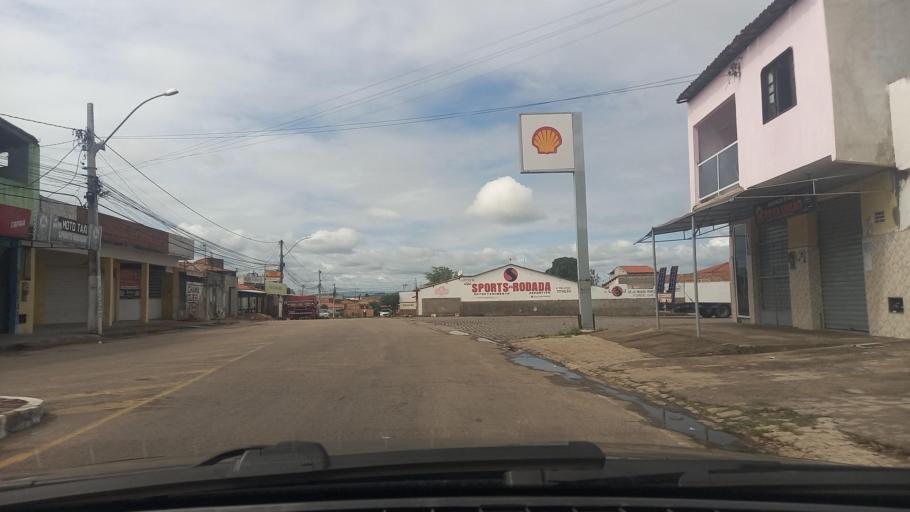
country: BR
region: Bahia
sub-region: Paulo Afonso
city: Paulo Afonso
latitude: -9.4373
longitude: -38.2056
